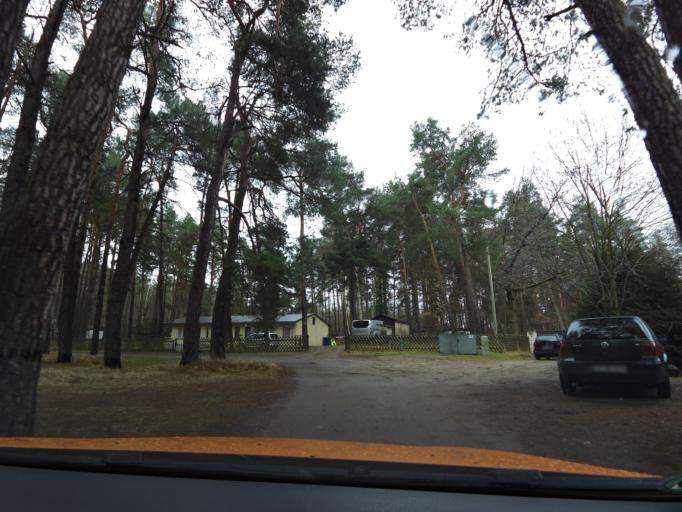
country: DE
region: Brandenburg
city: Sperenberg
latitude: 52.1629
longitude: 13.3650
